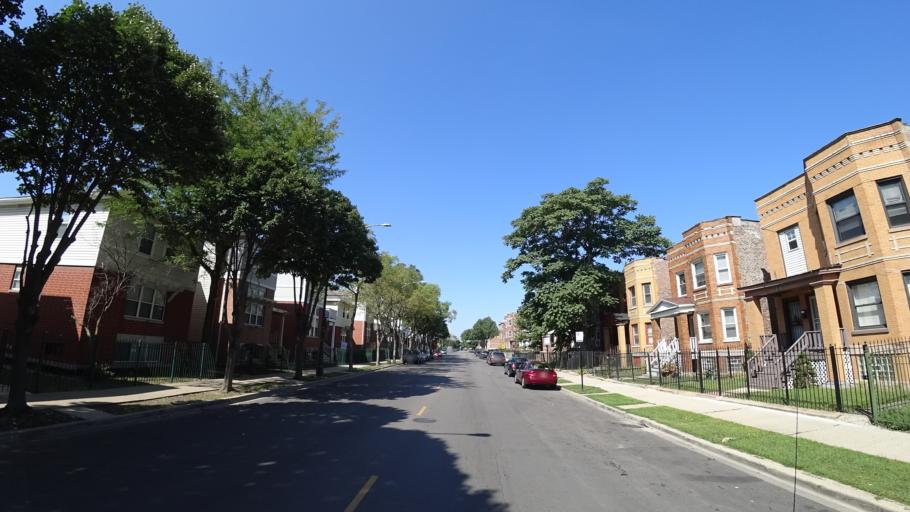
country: US
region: Illinois
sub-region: Cook County
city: Cicero
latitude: 41.8709
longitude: -87.7134
